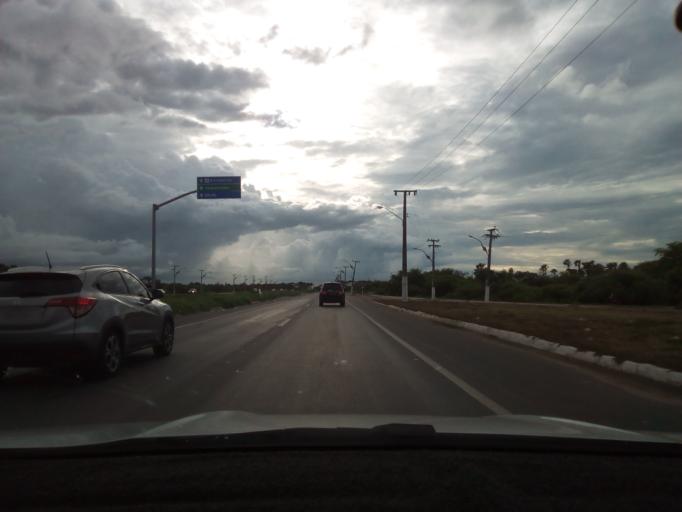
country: BR
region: Ceara
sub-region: Aracati
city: Aracati
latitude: -4.5787
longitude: -37.7798
